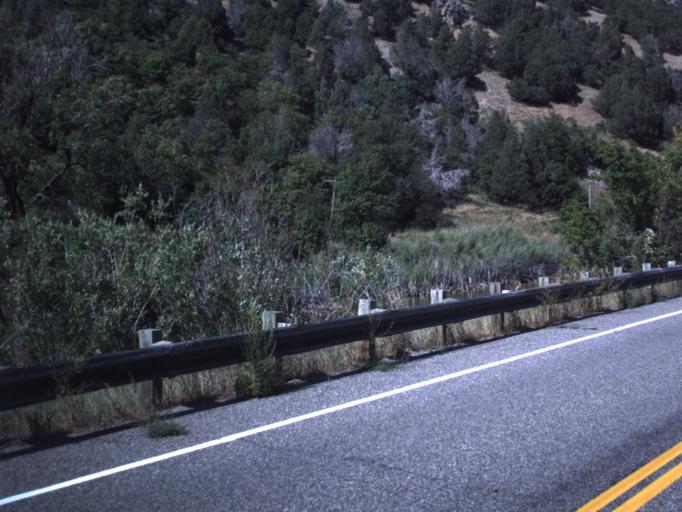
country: US
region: Utah
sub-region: Cache County
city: North Logan
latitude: 41.7552
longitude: -111.7143
